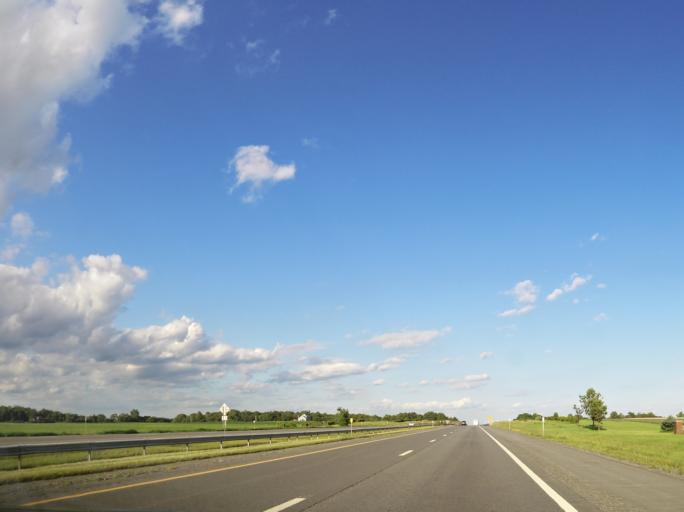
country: US
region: New York
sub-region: Genesee County
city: Batavia
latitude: 43.0218
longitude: -78.1416
